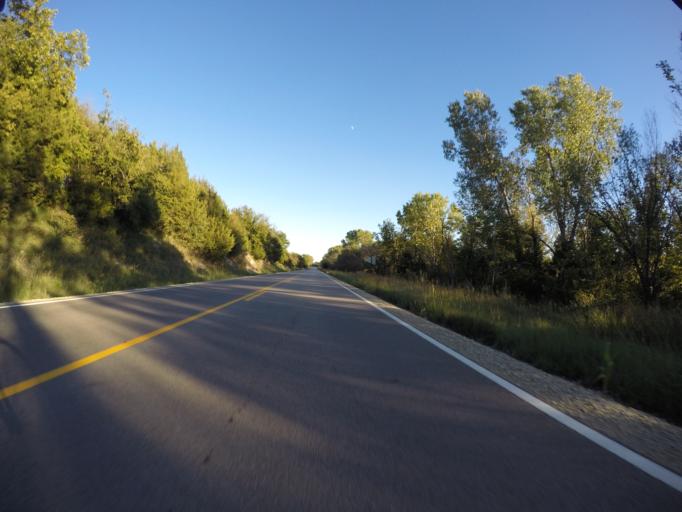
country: US
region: Kansas
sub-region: Riley County
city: Fort Riley North
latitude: 39.2435
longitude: -96.7654
